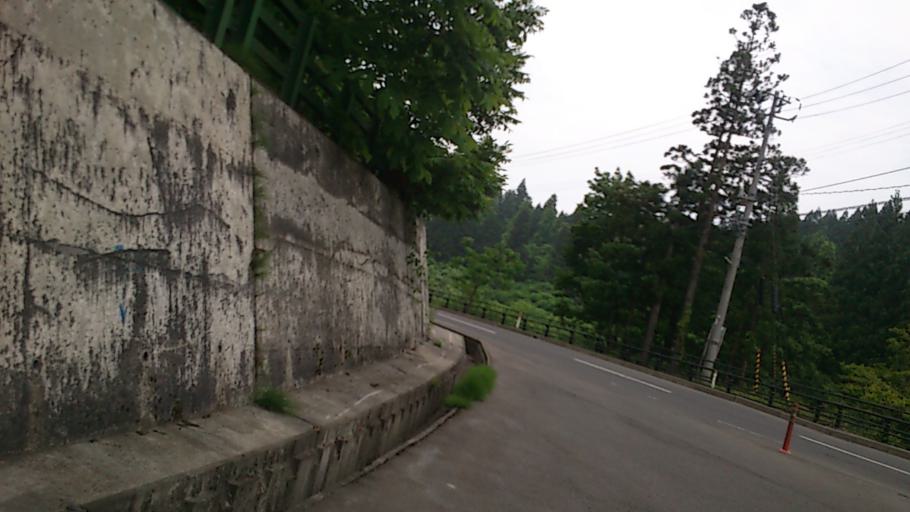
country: JP
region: Aomori
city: Hirosaki
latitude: 40.5695
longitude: 140.2952
